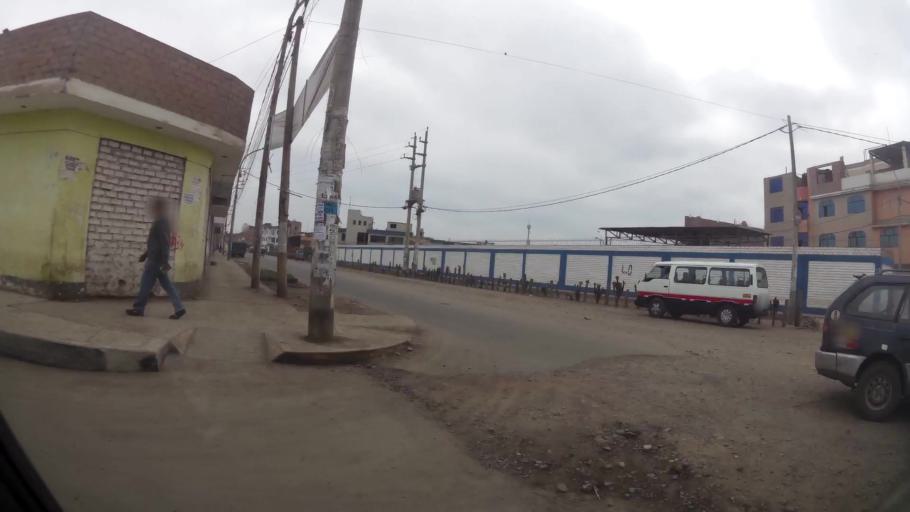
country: PE
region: Lima
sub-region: Provincia de Huaral
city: Huaral
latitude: -11.4965
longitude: -77.1999
